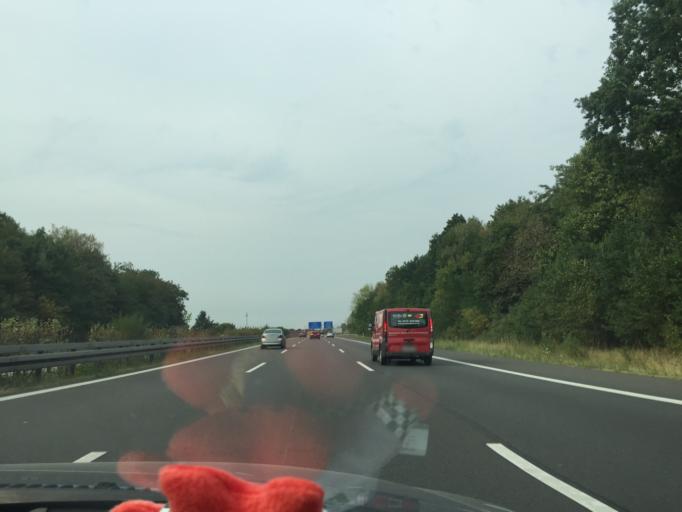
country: DE
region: Brandenburg
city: Woltersdorf
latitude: 52.4886
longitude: 13.7540
